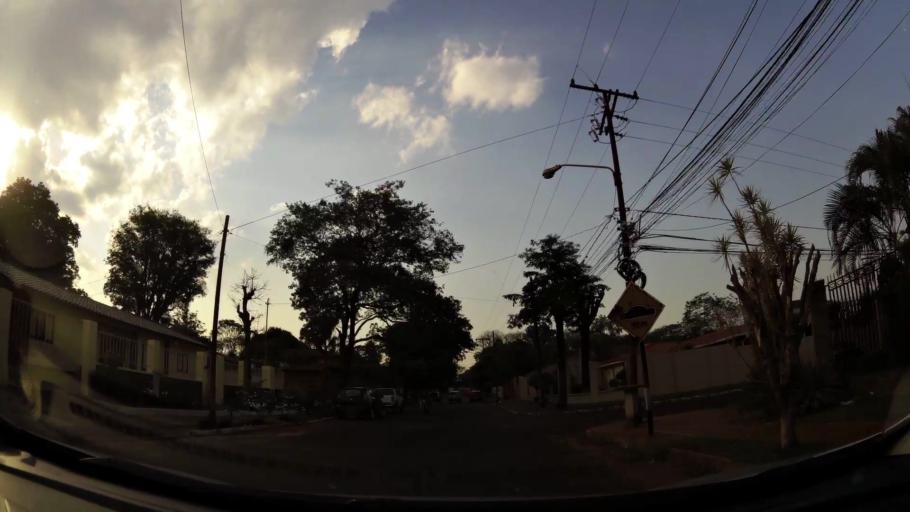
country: PY
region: Alto Parana
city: Presidente Franco
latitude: -25.5209
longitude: -54.6386
